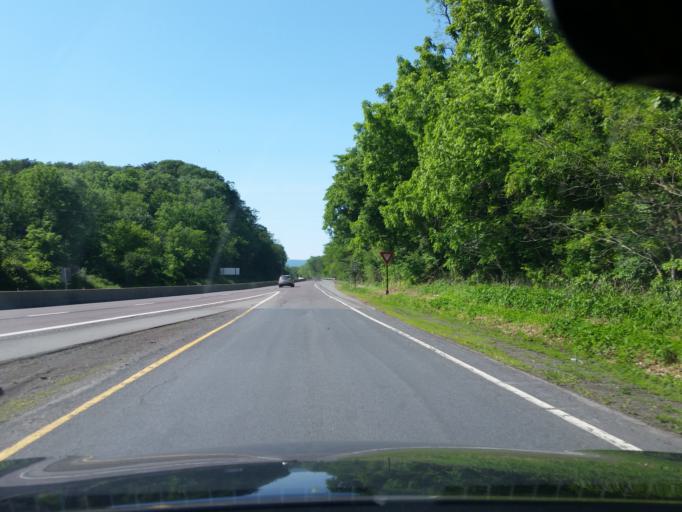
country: US
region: Pennsylvania
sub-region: Northumberland County
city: Watsontown
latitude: 41.0786
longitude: -76.8740
